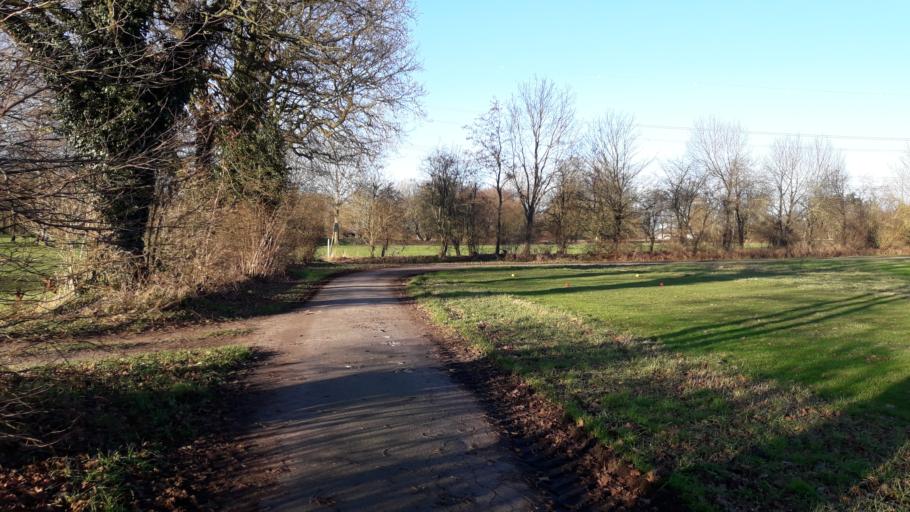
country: DE
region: Schleswig-Holstein
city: Quickborn
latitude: 53.7160
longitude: 9.8610
